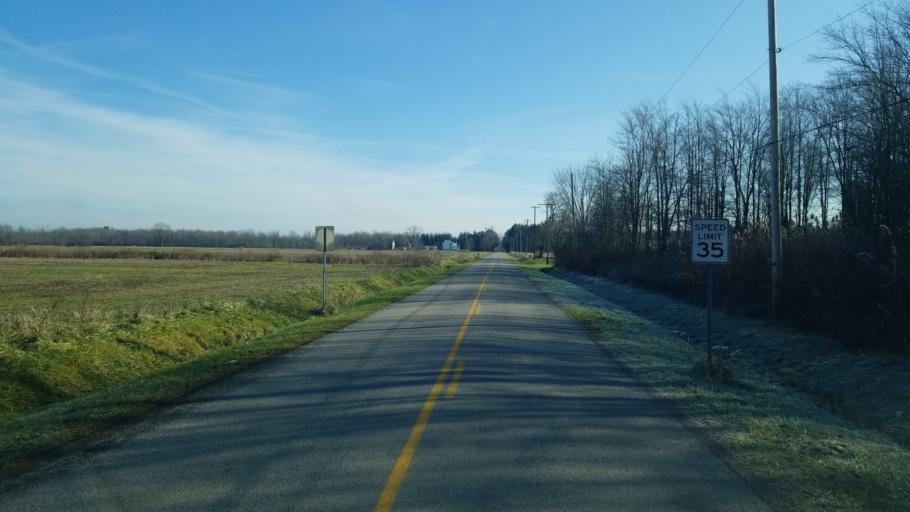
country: US
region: Ohio
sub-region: Ashtabula County
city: Jefferson
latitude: 41.7385
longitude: -80.7244
